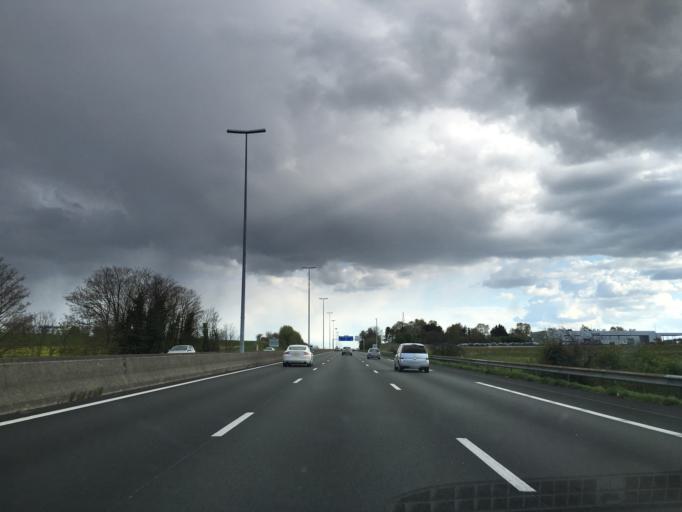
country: FR
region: Ile-de-France
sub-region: Departement du Val-d'Oise
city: Survilliers
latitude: 49.0941
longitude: 2.5502
